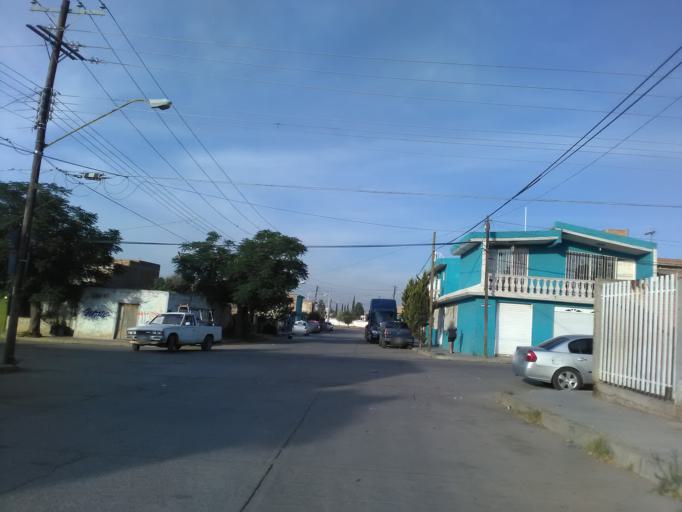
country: MX
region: Durango
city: Victoria de Durango
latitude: 24.0436
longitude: -104.6492
